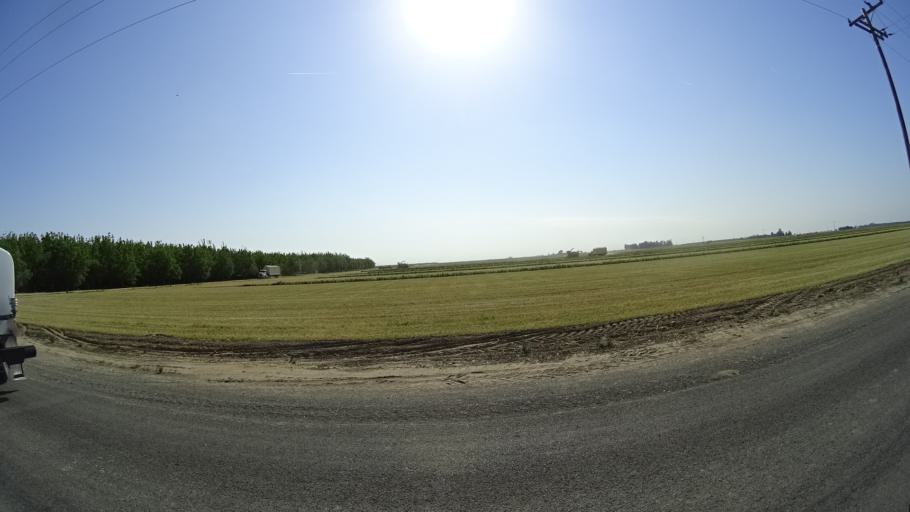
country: US
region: California
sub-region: Kings County
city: Home Garden
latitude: 36.3089
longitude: -119.5832
